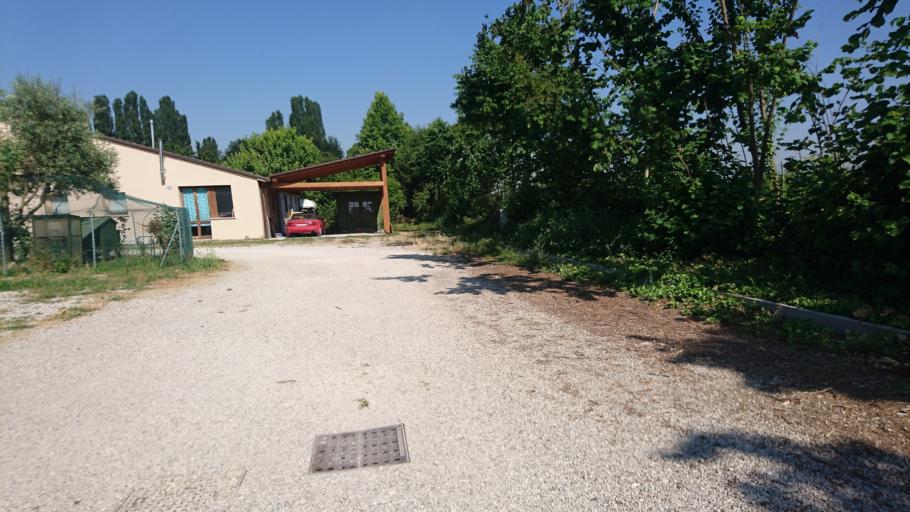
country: IT
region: Veneto
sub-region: Provincia di Padova
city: Tencarola
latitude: 45.3732
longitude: 11.8120
